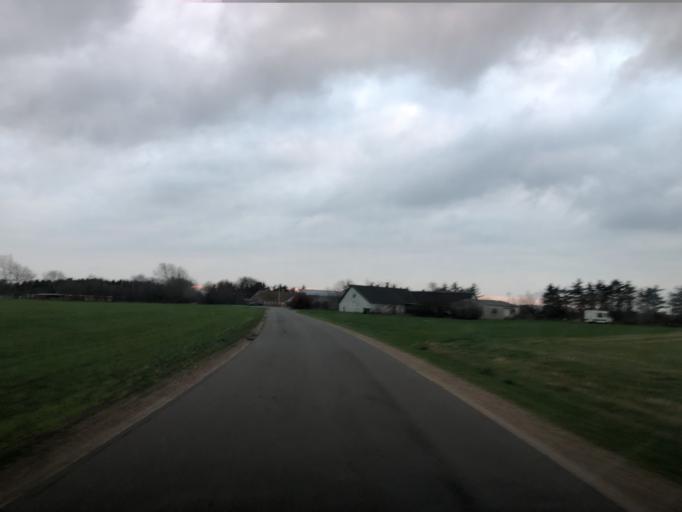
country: DK
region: Central Jutland
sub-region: Holstebro Kommune
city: Ulfborg
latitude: 56.2347
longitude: 8.2784
